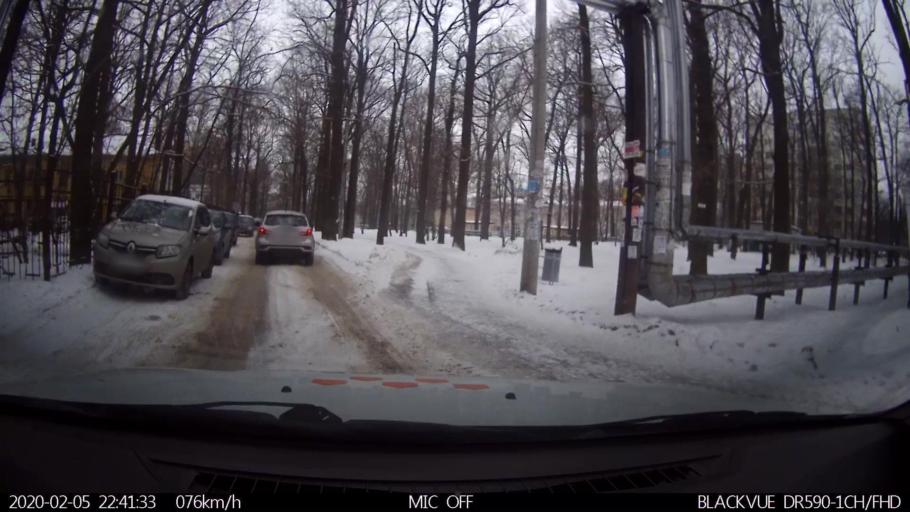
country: RU
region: Nizjnij Novgorod
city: Imeni Stepana Razina
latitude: 54.7205
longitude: 44.3398
